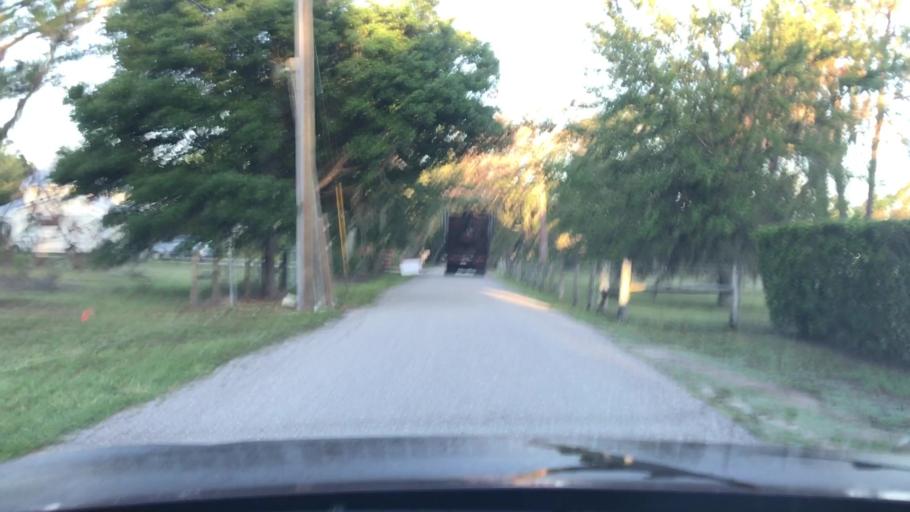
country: US
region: Florida
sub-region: Sarasota County
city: Lake Sarasota
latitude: 27.3309
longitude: -82.4102
